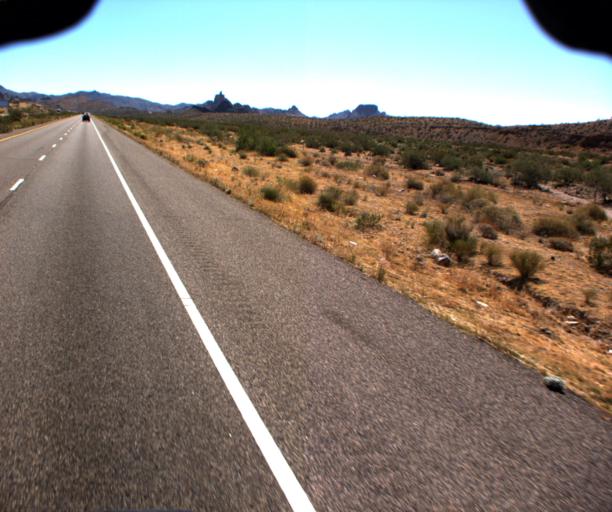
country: US
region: Nevada
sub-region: Clark County
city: Laughlin
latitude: 35.1853
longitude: -114.4762
